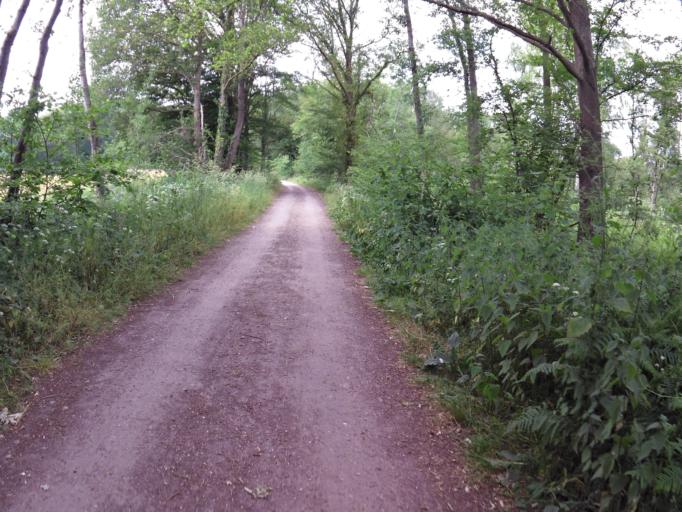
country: NL
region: North Brabant
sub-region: Gemeente Oirschot
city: Oirschot
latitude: 51.5348
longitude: 5.3495
